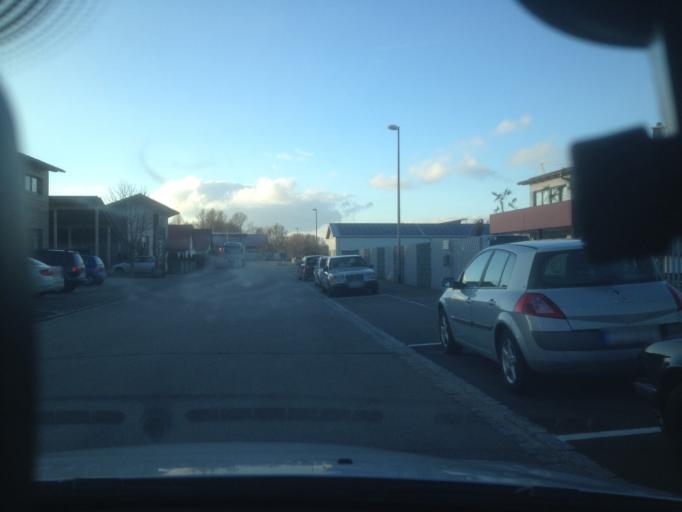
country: DE
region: Bavaria
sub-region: Upper Bavaria
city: Prittriching
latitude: 48.2126
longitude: 10.9308
